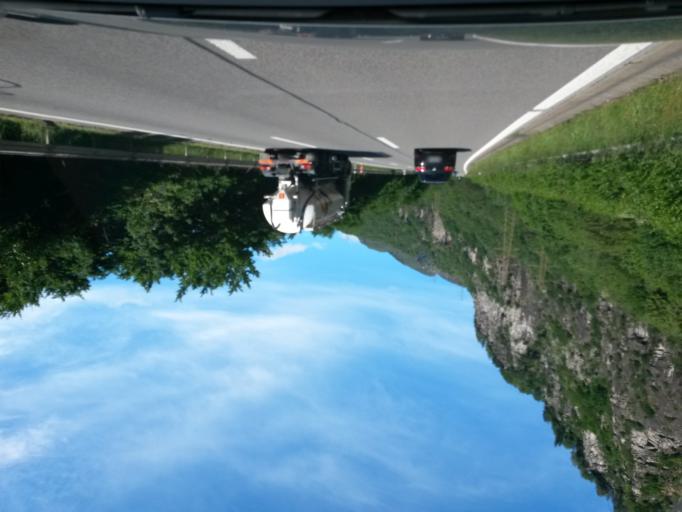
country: CH
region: Ticino
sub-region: Leventina District
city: Bodio
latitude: 46.3978
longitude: 8.8722
